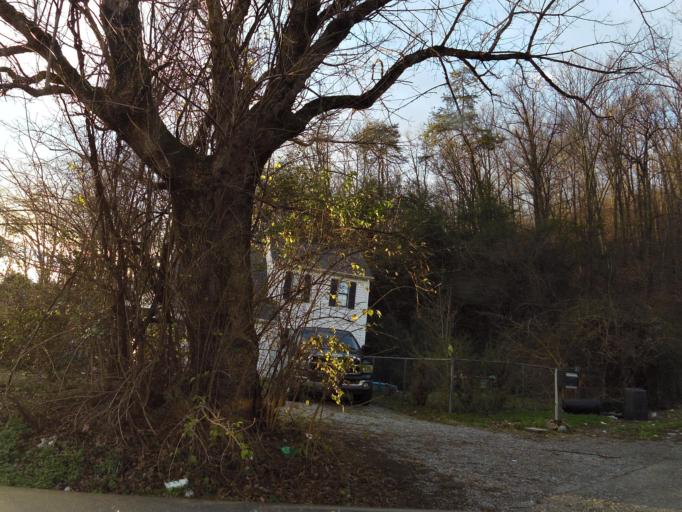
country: US
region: Tennessee
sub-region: Knox County
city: Knoxville
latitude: 35.9972
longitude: -83.9491
